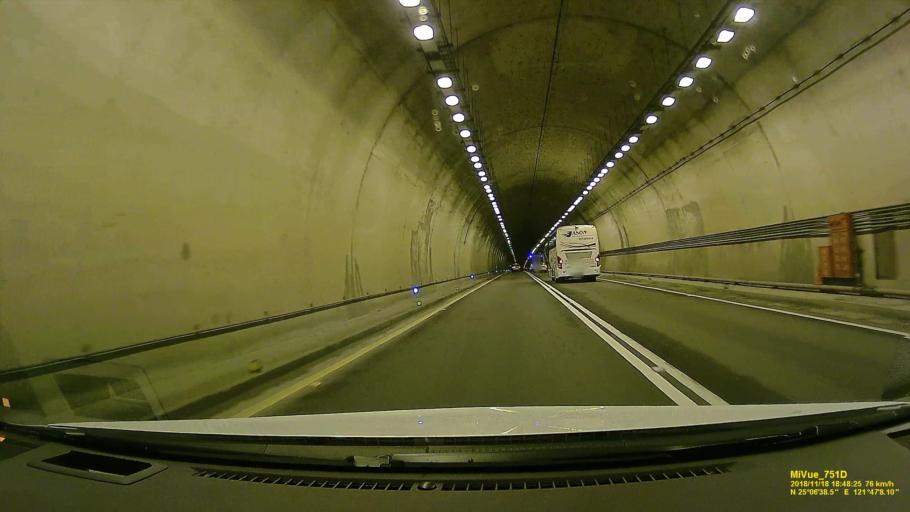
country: TW
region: Taiwan
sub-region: Keelung
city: Keelung
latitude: 25.1107
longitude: 121.7852
